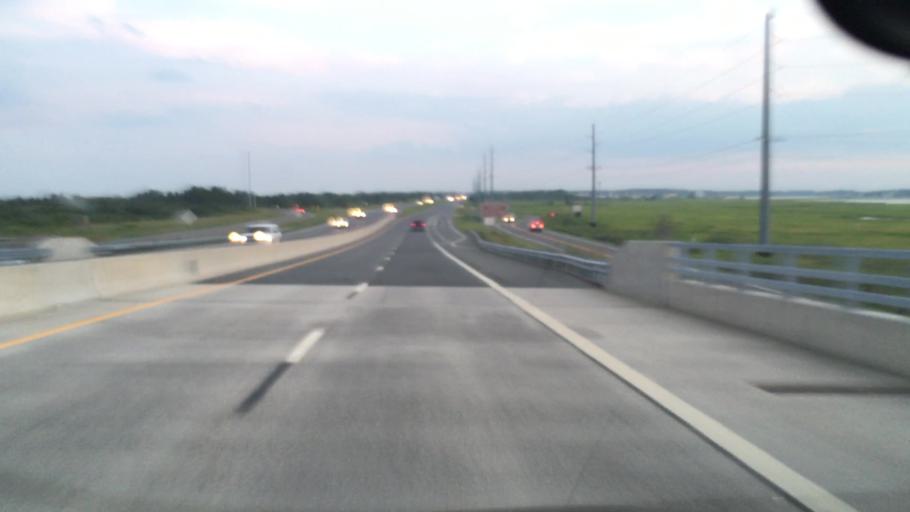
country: US
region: Delaware
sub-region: Sussex County
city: Ocean View
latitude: 38.6045
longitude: -75.0633
